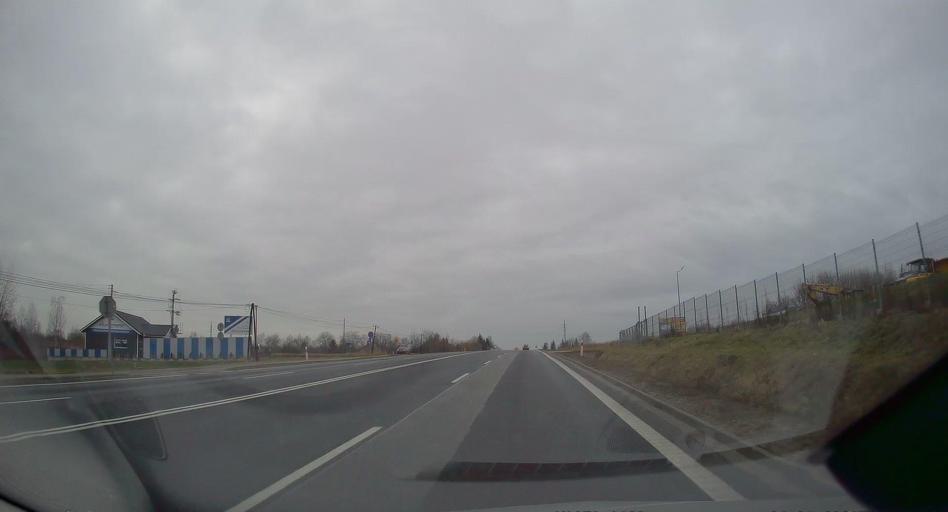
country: PL
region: Subcarpathian Voivodeship
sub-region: Powiat rzeszowski
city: Swilcza
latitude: 50.0679
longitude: 21.9184
